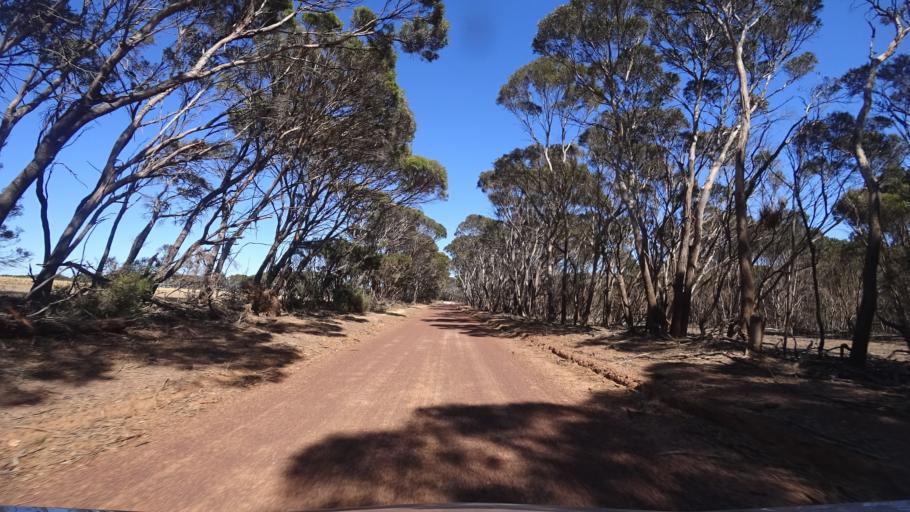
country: AU
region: South Australia
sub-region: Kangaroo Island
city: Kingscote
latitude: -35.7502
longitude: 137.7325
